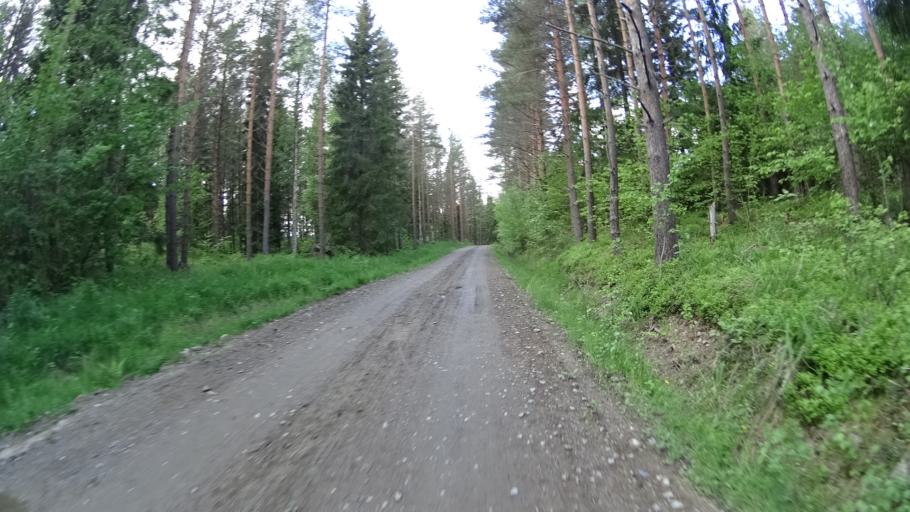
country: FI
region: Uusimaa
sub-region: Raaseporin
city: Karis
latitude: 60.1549
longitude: 23.6215
